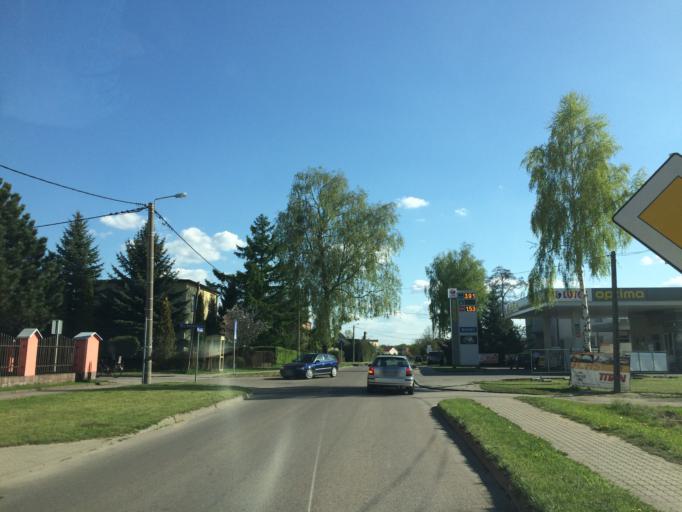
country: PL
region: Warmian-Masurian Voivodeship
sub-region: Powiat dzialdowski
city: Rybno
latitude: 53.3890
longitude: 19.9314
